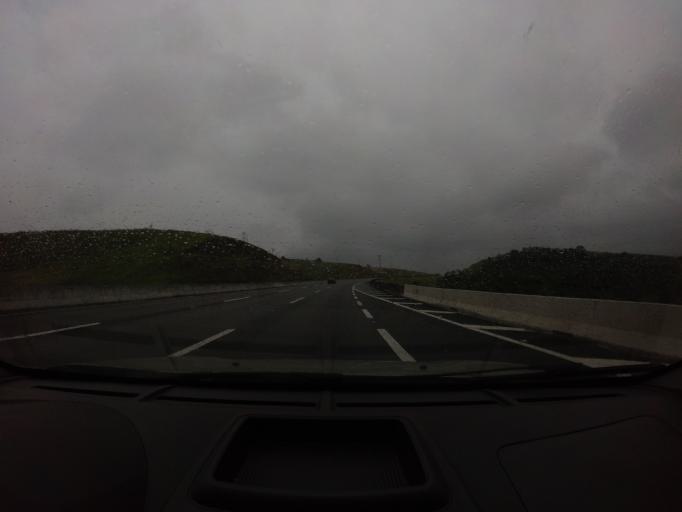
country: BR
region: Sao Paulo
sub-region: Santa Isabel
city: Santa Isabel
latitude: -23.2586
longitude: -46.0977
